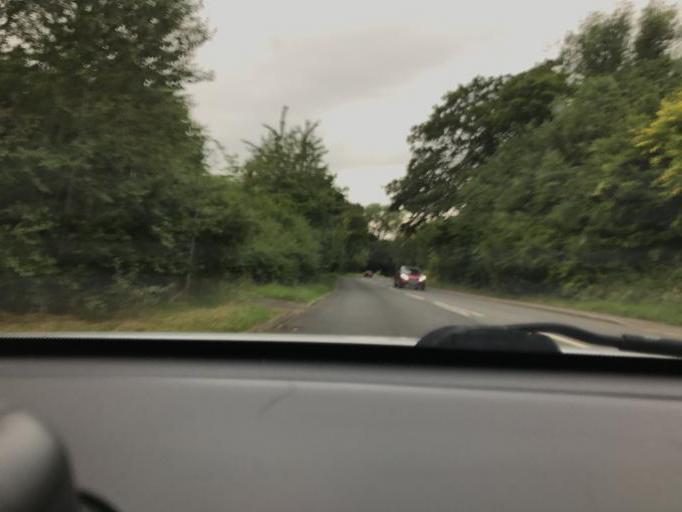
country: GB
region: England
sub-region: Cheshire West and Chester
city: Winsford
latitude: 53.2181
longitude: -2.5039
